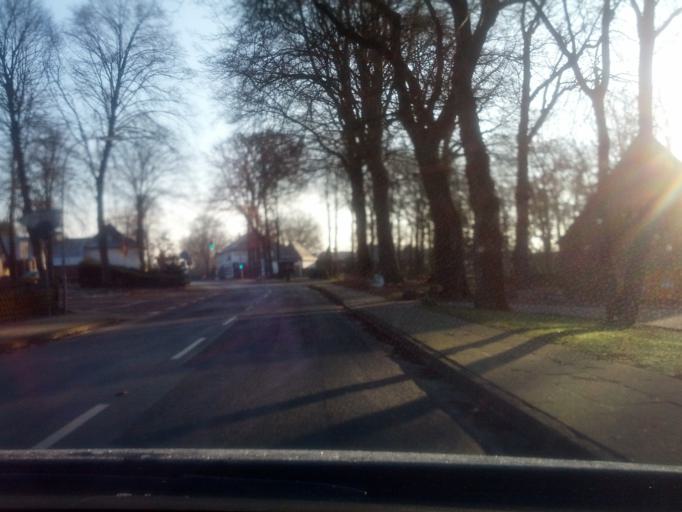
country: DE
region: Lower Saxony
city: Heidenau
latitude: 53.3152
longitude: 9.6488
